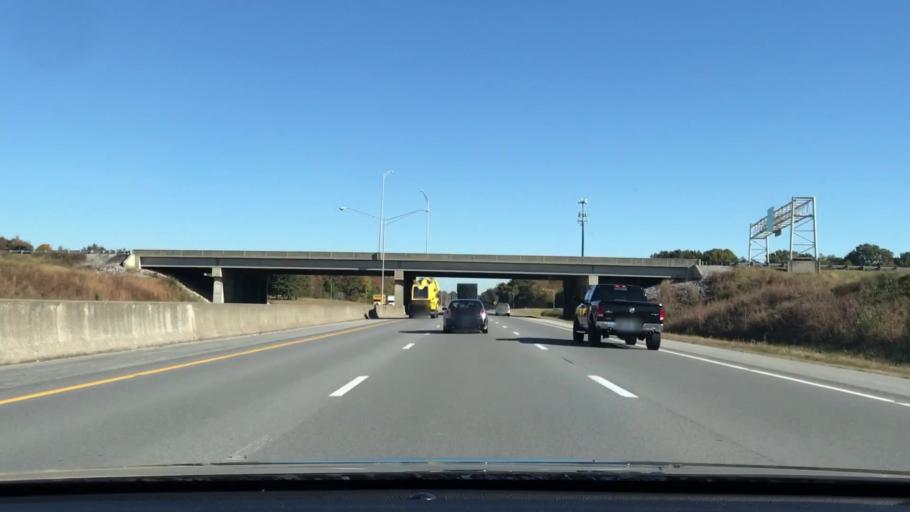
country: US
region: Kentucky
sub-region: Warren County
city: Bowling Green
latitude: 36.9767
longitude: -86.3914
